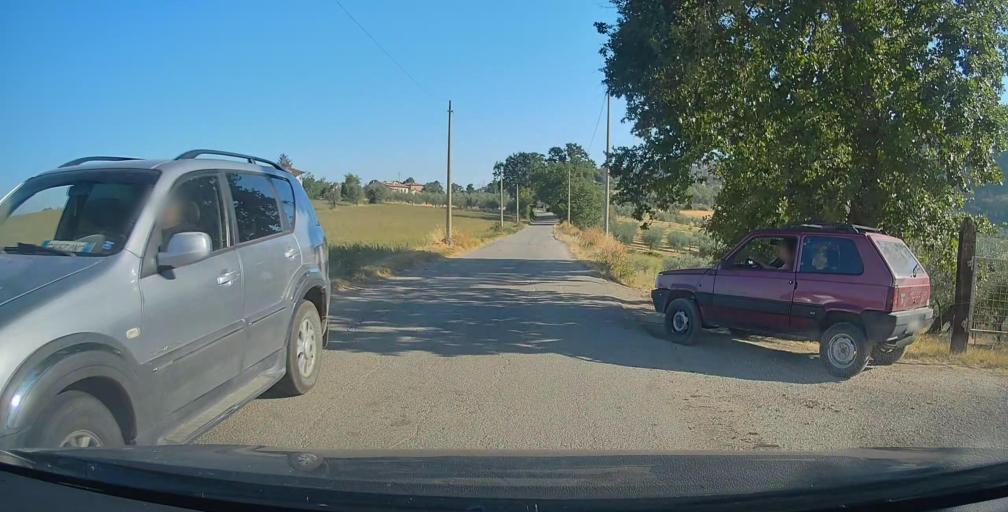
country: IT
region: Umbria
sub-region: Provincia di Terni
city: Calvi dell'Umbria
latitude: 42.3882
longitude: 12.5675
